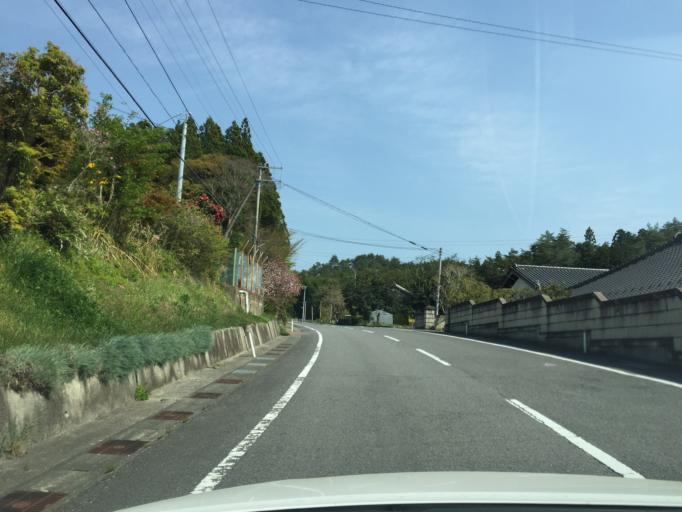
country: JP
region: Fukushima
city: Iwaki
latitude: 37.1681
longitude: 140.8508
